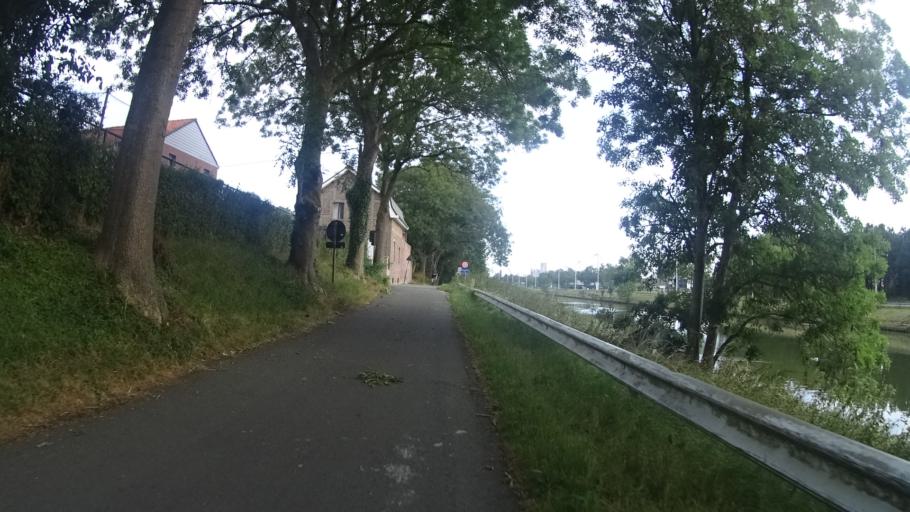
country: BE
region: Flanders
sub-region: Provincie West-Vlaanderen
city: Ieper
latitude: 50.8640
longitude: 2.8797
